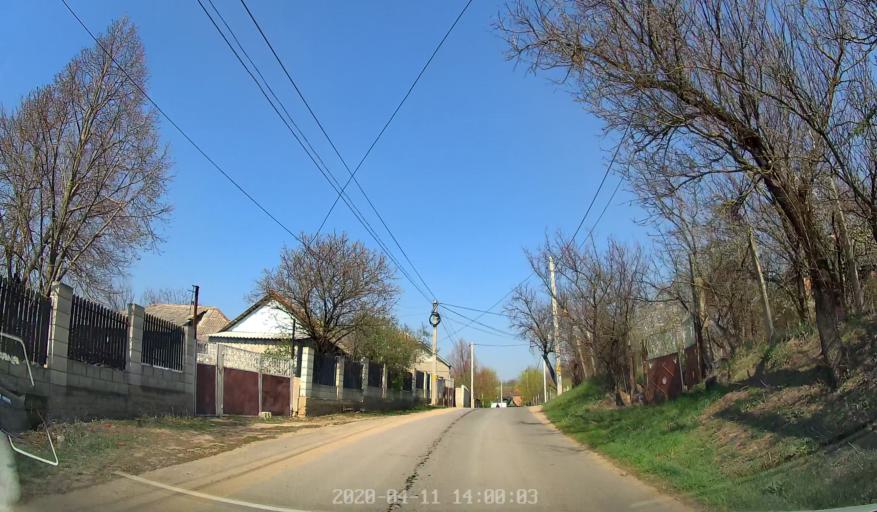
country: MD
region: Chisinau
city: Vadul lui Voda
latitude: 47.0838
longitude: 29.1324
